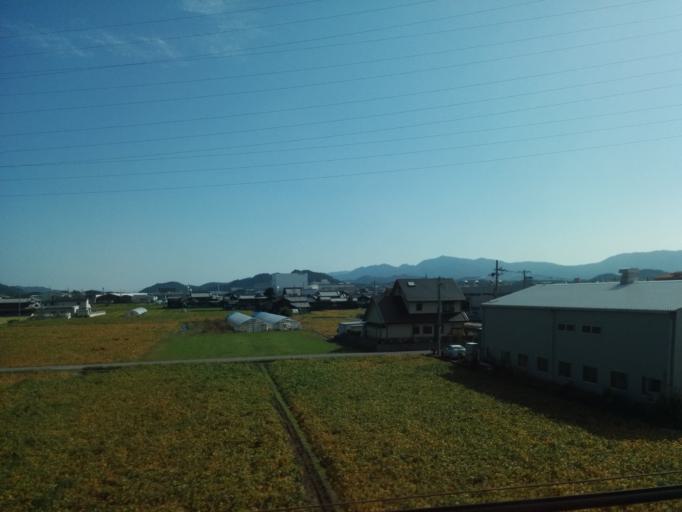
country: JP
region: Shiga Prefecture
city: Moriyama
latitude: 35.0412
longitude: 136.0016
